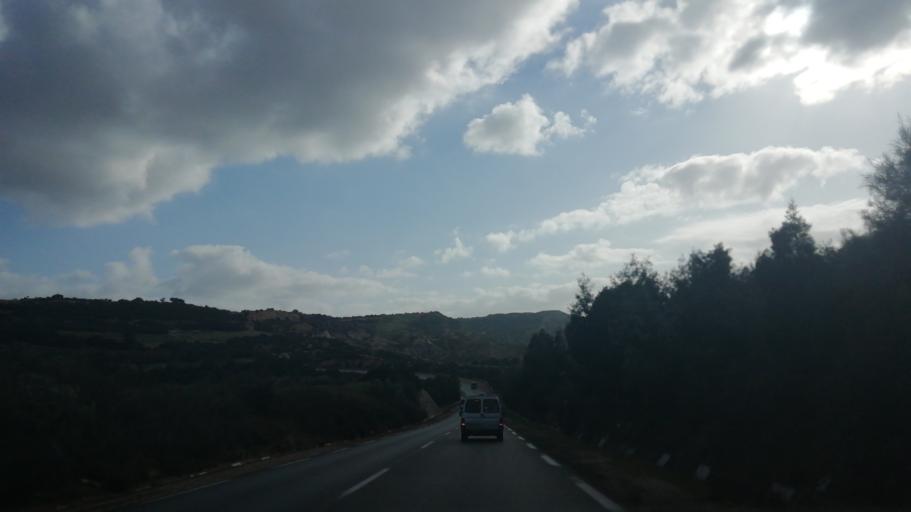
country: DZ
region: Relizane
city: Mazouna
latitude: 36.2376
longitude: 0.5384
